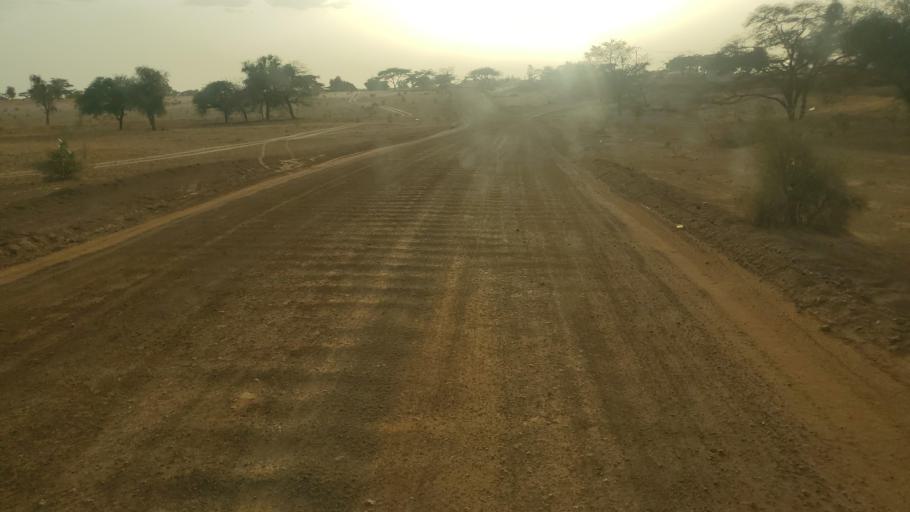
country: SN
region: Louga
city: Dara
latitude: 15.3638
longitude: -15.5535
